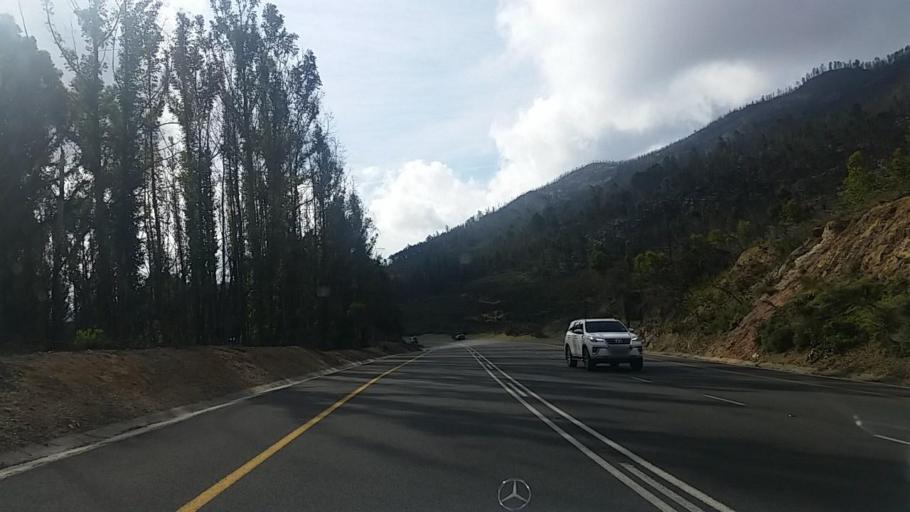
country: ZA
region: Western Cape
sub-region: Eden District Municipality
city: George
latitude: -33.8776
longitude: 22.3860
